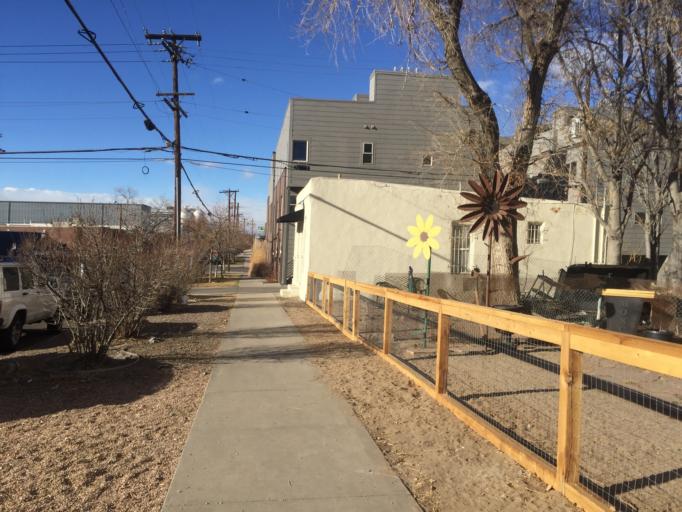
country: US
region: Colorado
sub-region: Denver County
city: Denver
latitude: 39.7655
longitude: -104.9749
